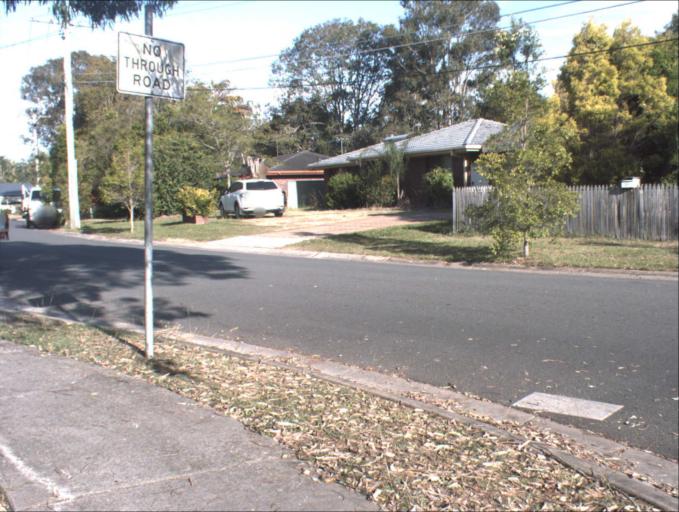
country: AU
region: Queensland
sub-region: Logan
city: Beenleigh
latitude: -27.6828
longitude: 153.1839
